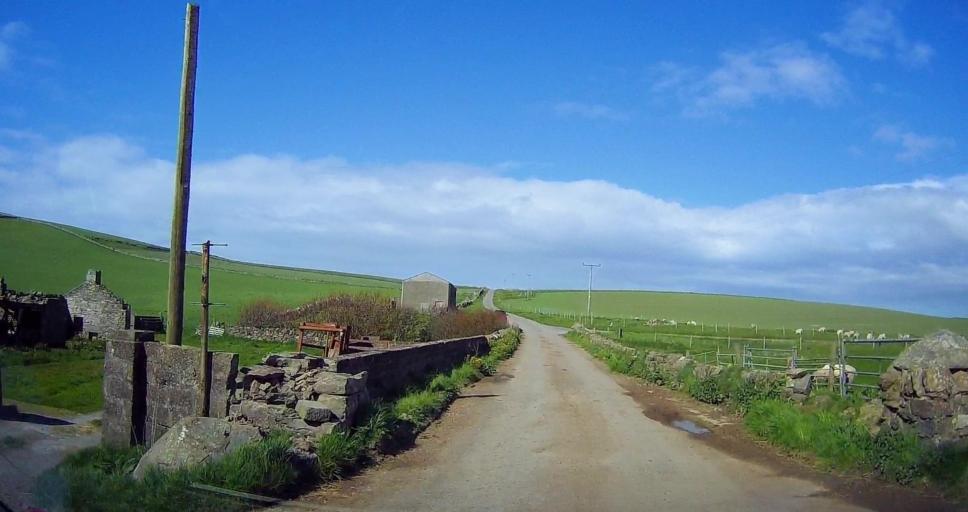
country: GB
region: Scotland
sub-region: Shetland Islands
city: Sandwick
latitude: 59.9022
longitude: -1.3382
